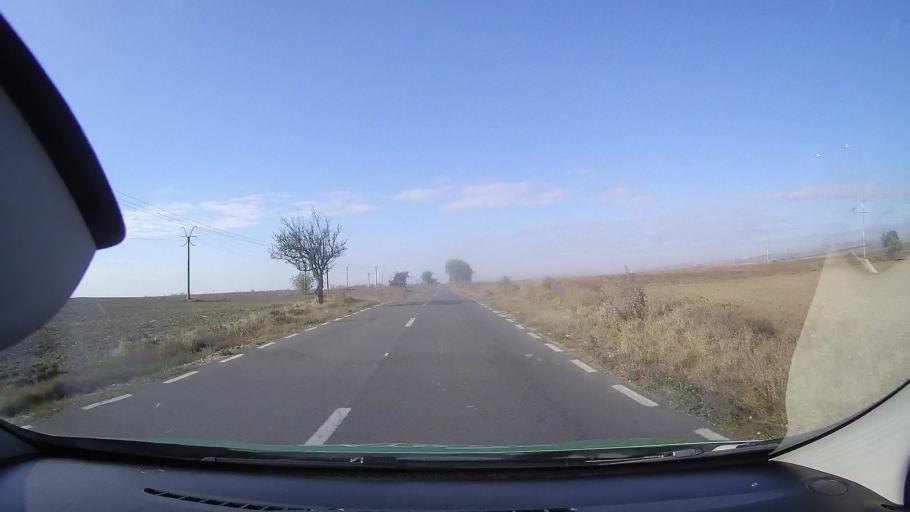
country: RO
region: Tulcea
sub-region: Comuna Murighiol
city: Murighiol
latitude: 45.0282
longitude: 29.1464
